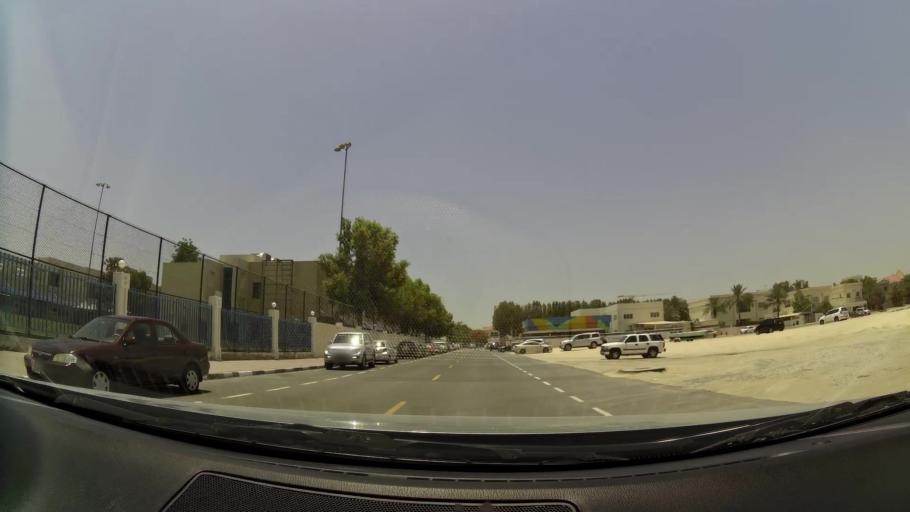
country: AE
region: Dubai
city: Dubai
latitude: 25.1763
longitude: 55.2393
